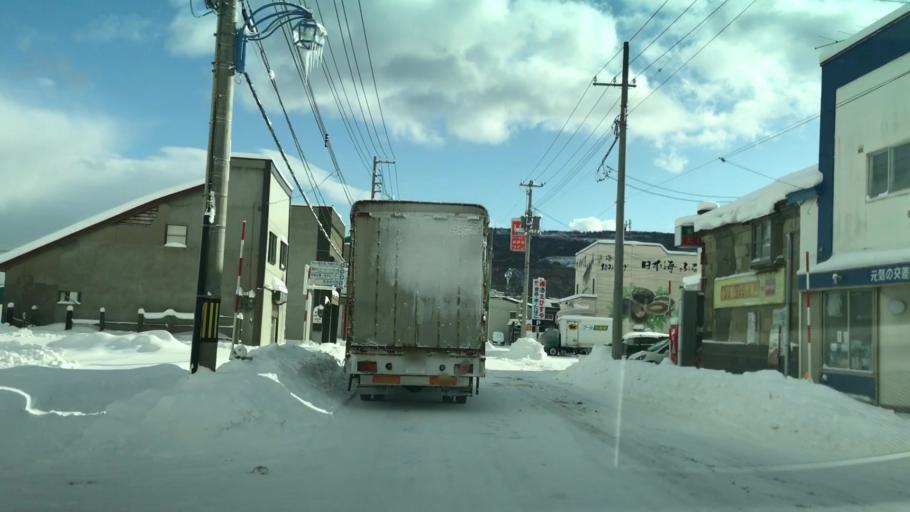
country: JP
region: Hokkaido
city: Yoichi
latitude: 43.2639
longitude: 140.6420
